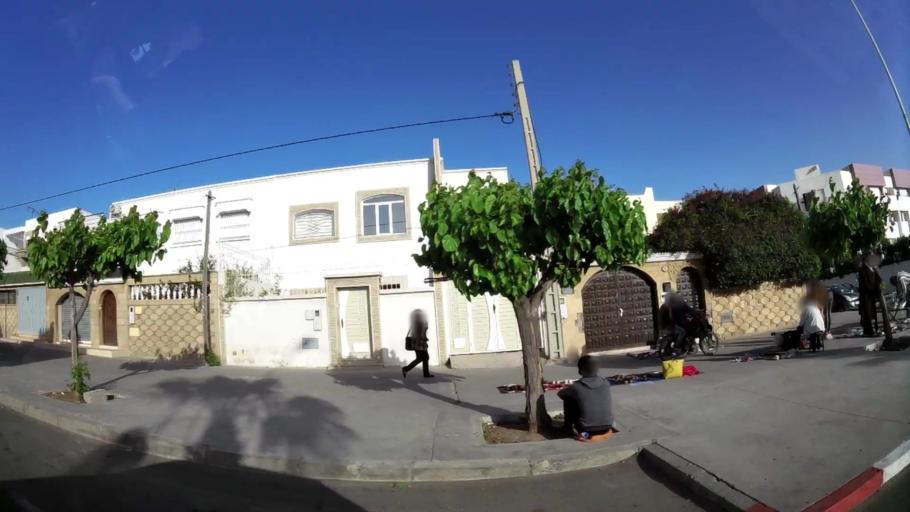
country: MA
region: Oued ed Dahab-Lagouira
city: Dakhla
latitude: 30.4072
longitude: -9.5503
